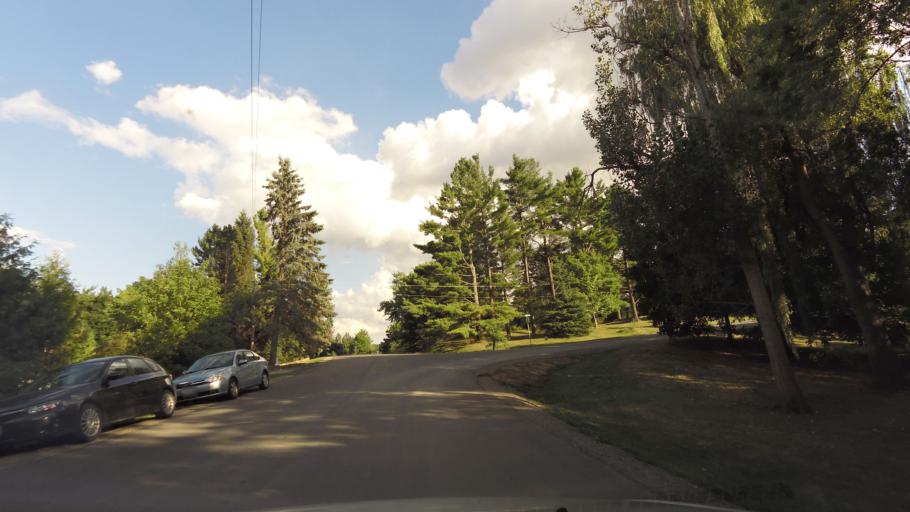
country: CA
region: Ontario
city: Brampton
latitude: 43.7651
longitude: -79.9247
